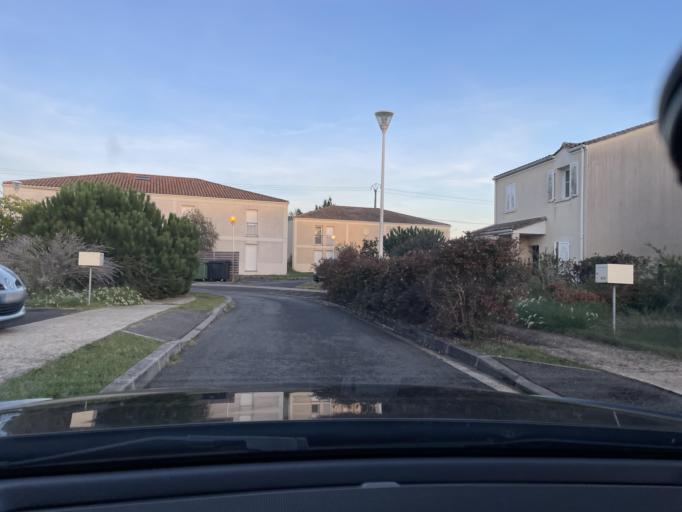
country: FR
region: Aquitaine
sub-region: Departement de la Gironde
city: Villenave-d'Ornon
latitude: 44.7795
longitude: -0.5409
